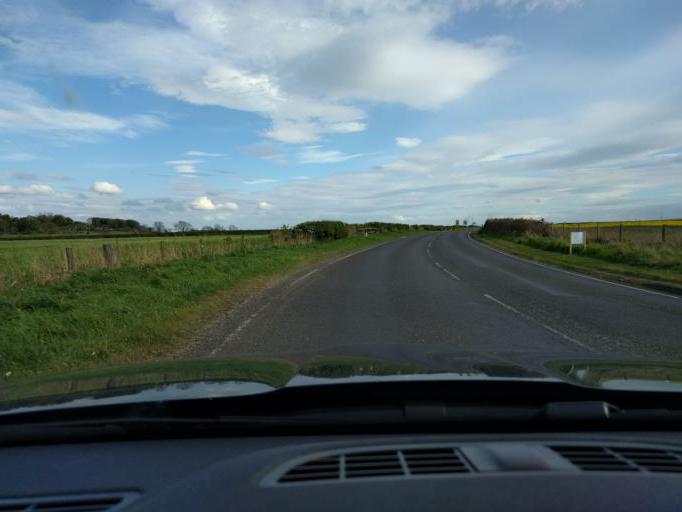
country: GB
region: England
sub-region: Northumberland
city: Stannington
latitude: 55.1334
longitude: -1.6469
